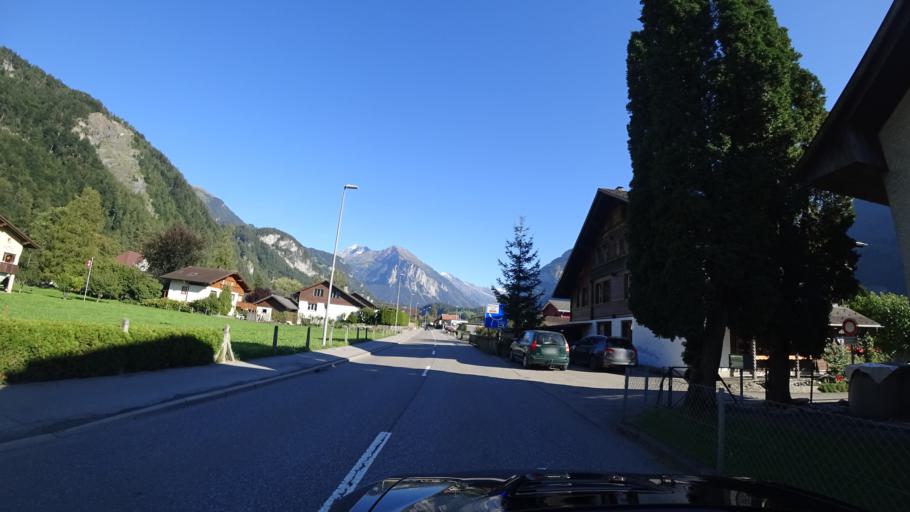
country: CH
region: Bern
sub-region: Interlaken-Oberhasli District
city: Meiringen
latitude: 46.7315
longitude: 8.1769
